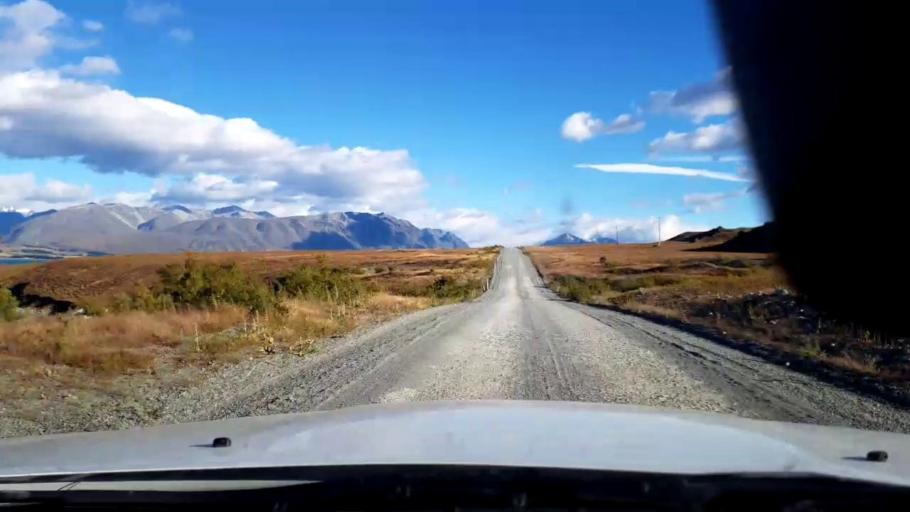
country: NZ
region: Canterbury
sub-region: Timaru District
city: Pleasant Point
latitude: -43.9247
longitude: 170.5600
